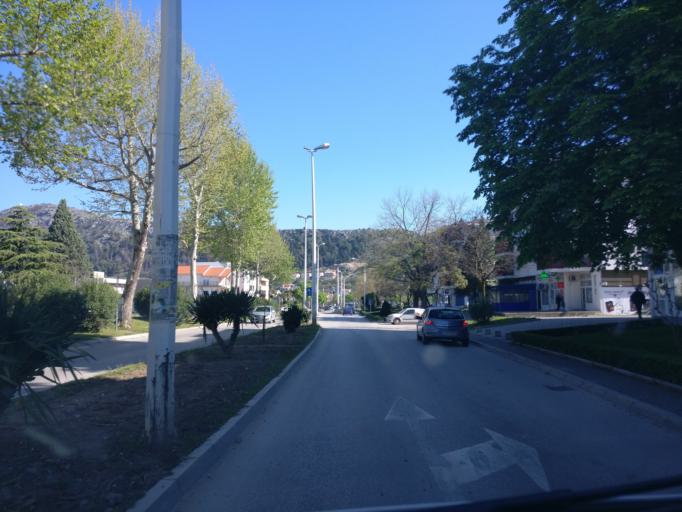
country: BA
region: Federation of Bosnia and Herzegovina
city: Capljina
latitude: 43.1102
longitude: 17.6992
